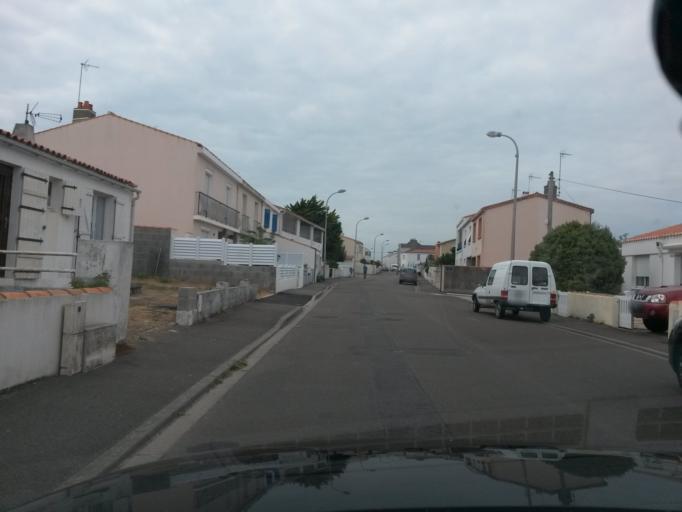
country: FR
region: Pays de la Loire
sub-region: Departement de la Vendee
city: Les Sables-d'Olonne
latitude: 46.5000
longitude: -1.7992
